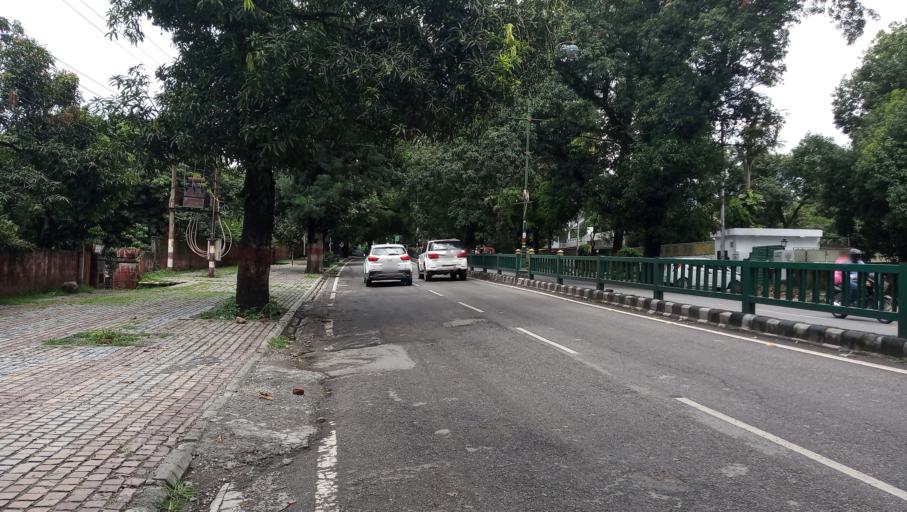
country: IN
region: Uttarakhand
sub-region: Dehradun
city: Dehradun
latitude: 30.3671
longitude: 78.0719
